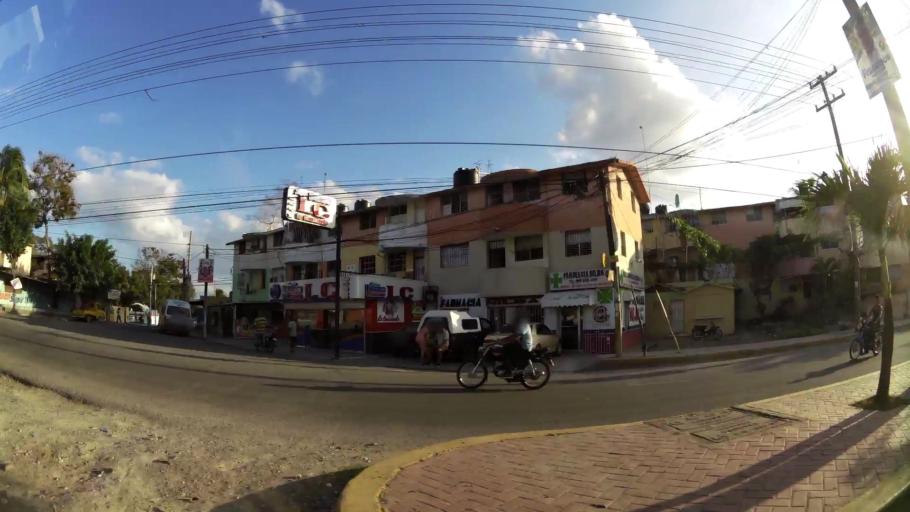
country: DO
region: Nacional
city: La Agustina
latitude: 18.5447
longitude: -69.9277
